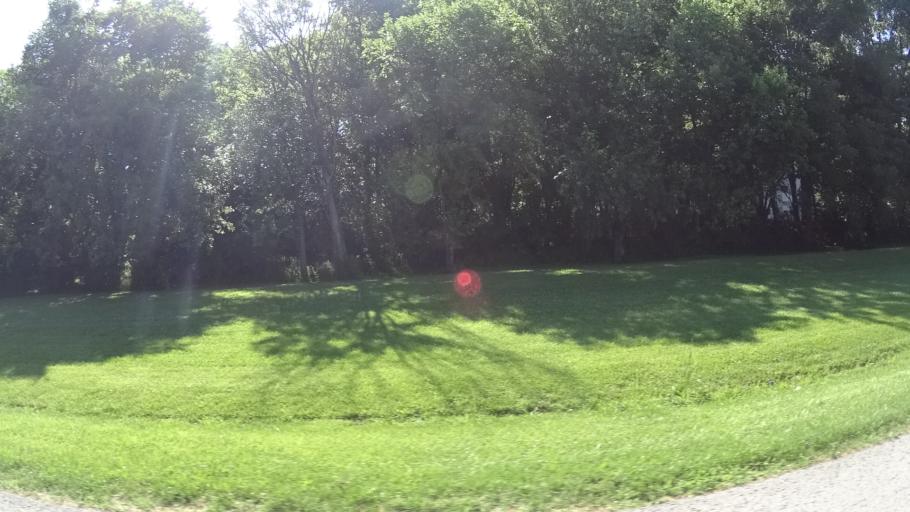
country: US
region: Indiana
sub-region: Madison County
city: Pendleton
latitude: 39.9872
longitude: -85.7531
